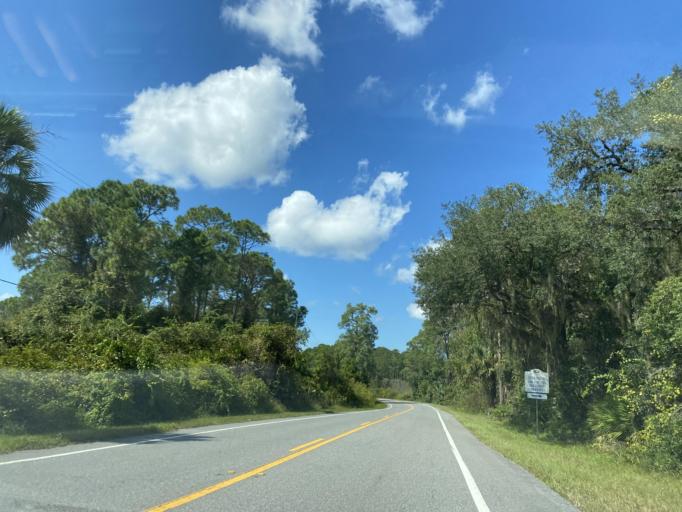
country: US
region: Florida
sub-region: Lake County
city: Lake Mack-Forest Hills
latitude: 29.0131
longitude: -81.4600
